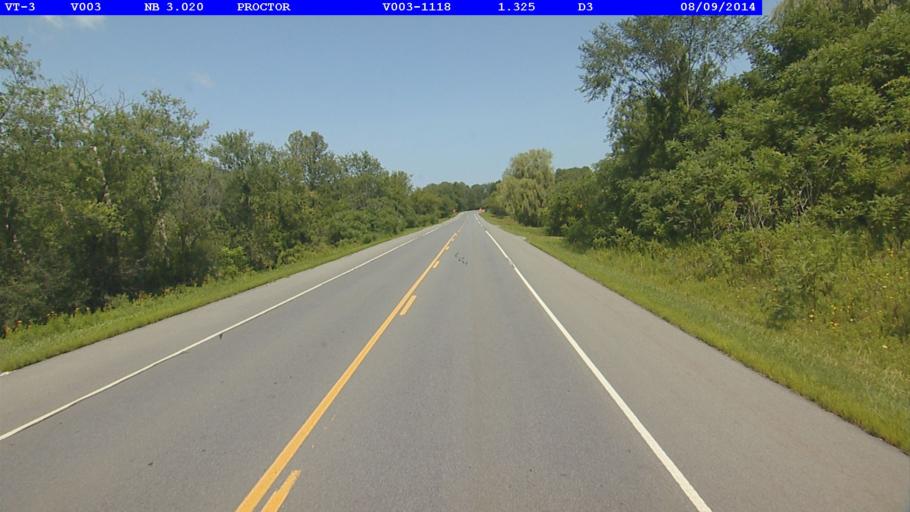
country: US
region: Vermont
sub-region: Rutland County
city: West Rutland
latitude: 43.6429
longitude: -73.0327
